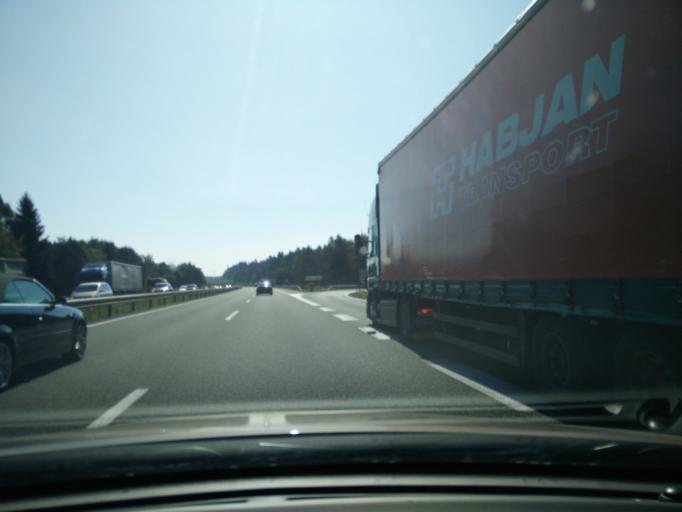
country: SI
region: Naklo
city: Naklo
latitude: 46.2681
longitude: 14.3341
